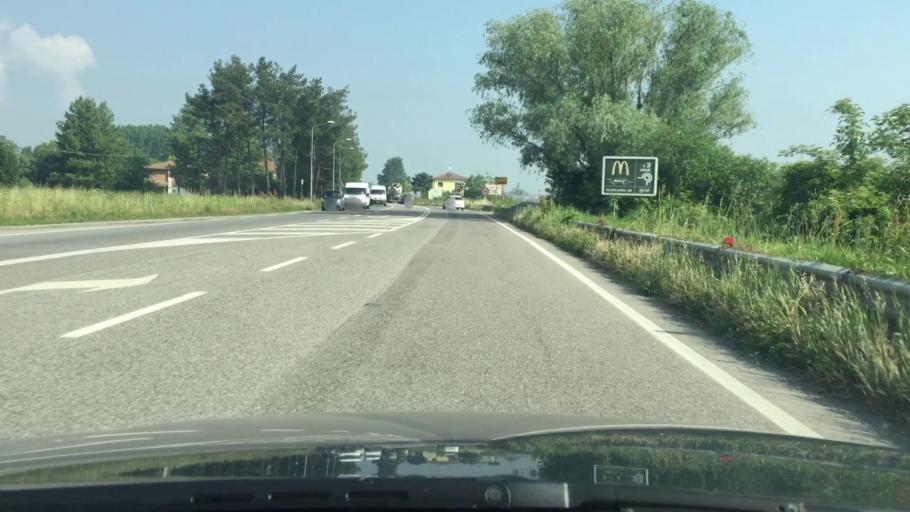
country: IT
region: Emilia-Romagna
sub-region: Provincia di Ferrara
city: Gaibanella-Sant'Edigio
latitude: 44.8058
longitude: 11.6362
